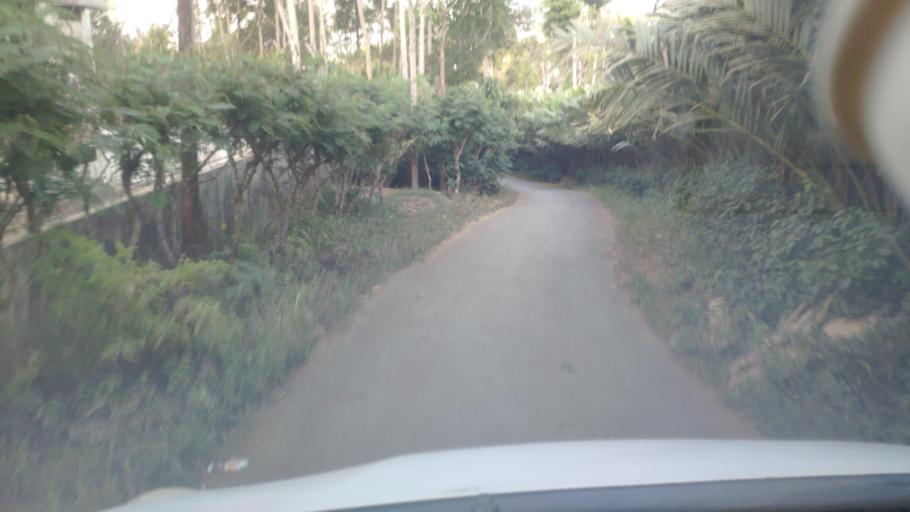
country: ID
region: Central Java
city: Wonosobo
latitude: -7.4353
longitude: 109.7542
